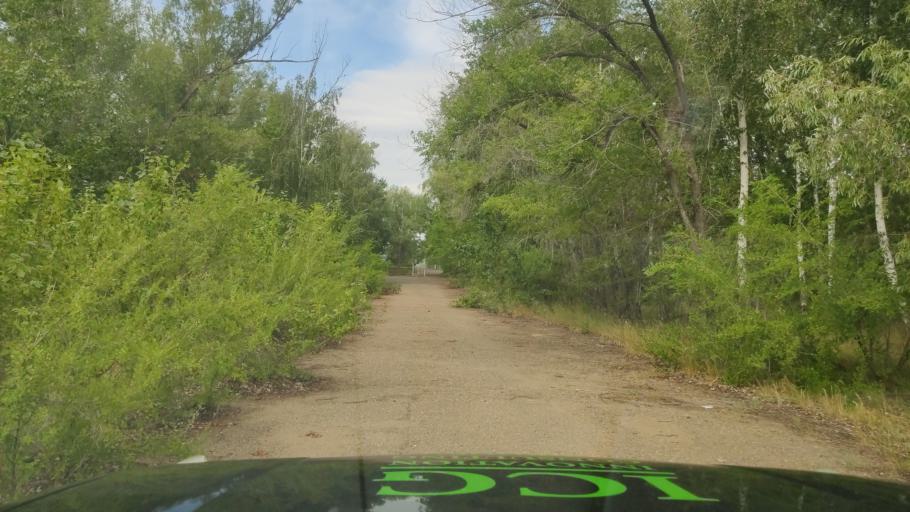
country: KZ
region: Pavlodar
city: Leninskiy
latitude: 52.4976
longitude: 76.8195
